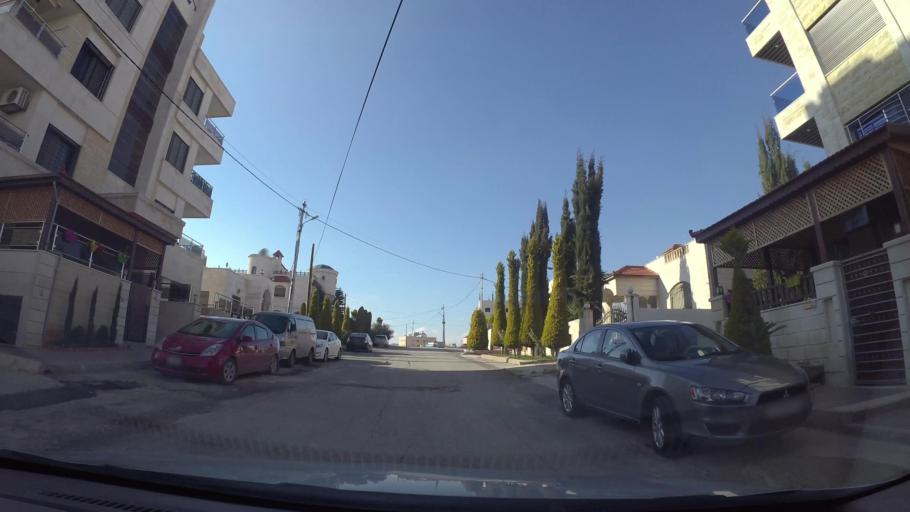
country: JO
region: Amman
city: Al Bunayyat ash Shamaliyah
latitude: 31.8995
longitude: 35.9232
